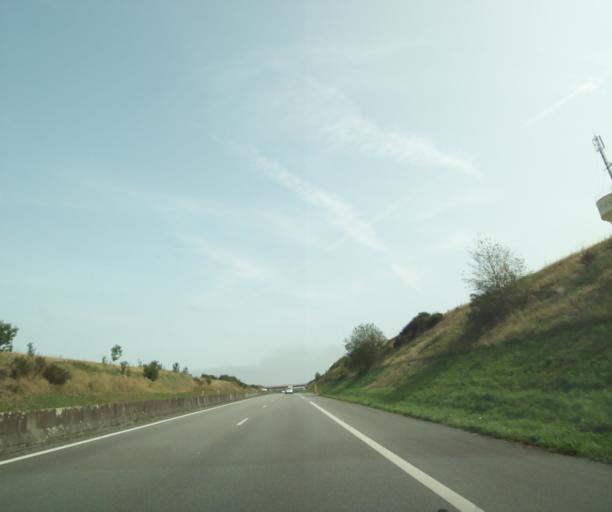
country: FR
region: Lower Normandy
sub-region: Departement de l'Orne
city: Radon
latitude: 48.5345
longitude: 0.1627
